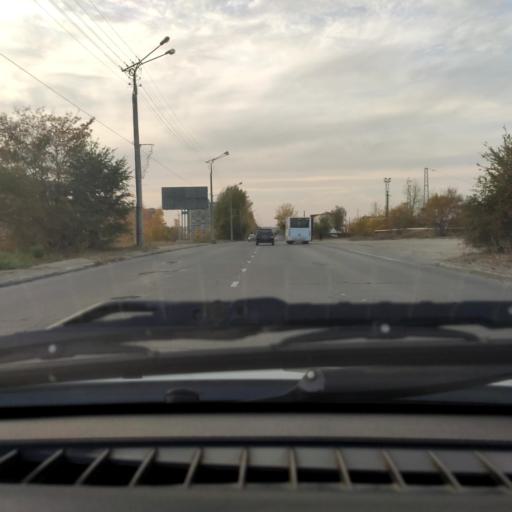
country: RU
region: Samara
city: Zhigulevsk
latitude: 53.4752
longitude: 49.5312
